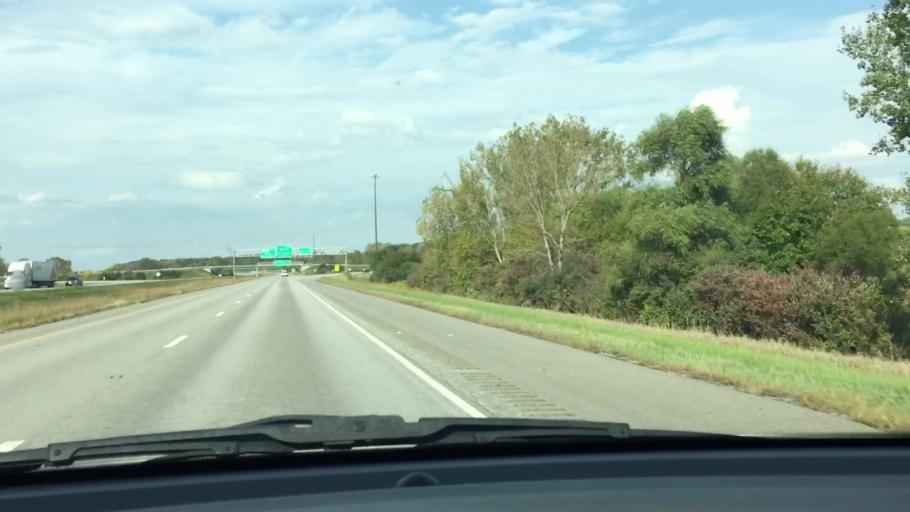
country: US
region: Illinois
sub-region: Henry County
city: Colona
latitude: 41.5349
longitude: -90.3196
